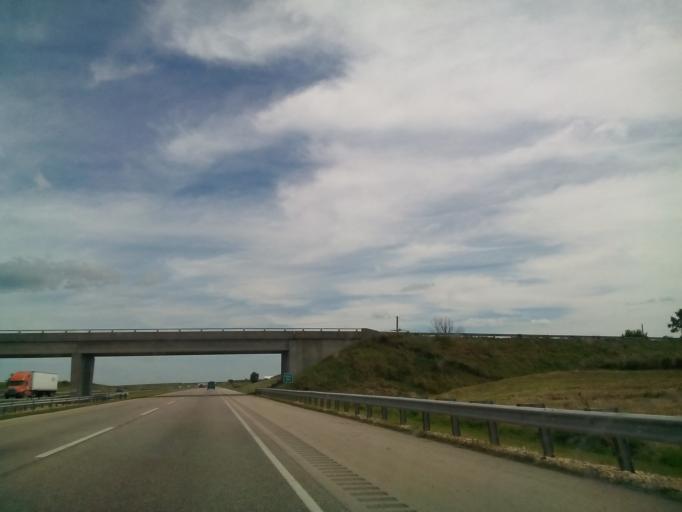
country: US
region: Illinois
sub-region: DeKalb County
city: Malta
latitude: 41.8994
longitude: -88.9267
